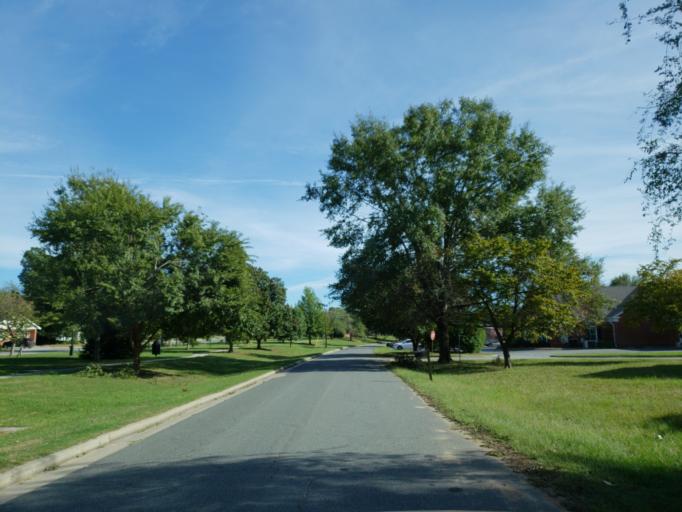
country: US
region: Georgia
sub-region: Crawford County
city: Roberta
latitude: 32.7214
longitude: -84.0120
